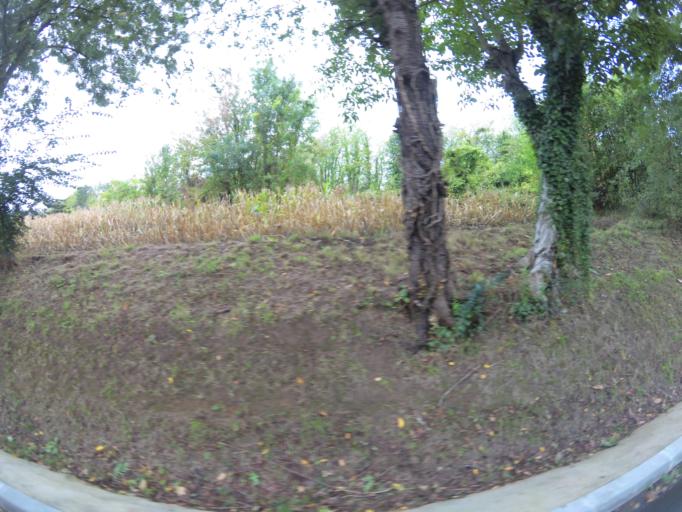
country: FR
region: Ile-de-France
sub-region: Departement de Seine-et-Marne
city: Dampmart
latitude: 48.8769
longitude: 2.7325
